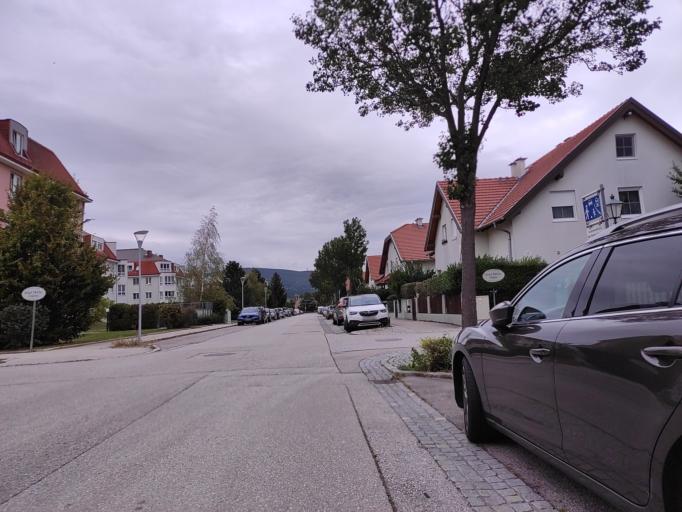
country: AT
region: Lower Austria
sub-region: Politischer Bezirk Baden
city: Pfaffstatten
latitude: 48.0036
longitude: 16.2563
